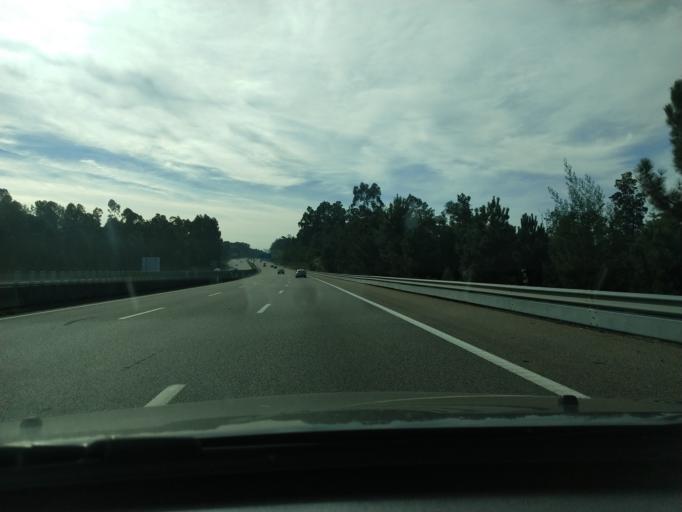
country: PT
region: Aveiro
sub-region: Santa Maria da Feira
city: Rio Meao
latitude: 40.9377
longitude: -8.5735
